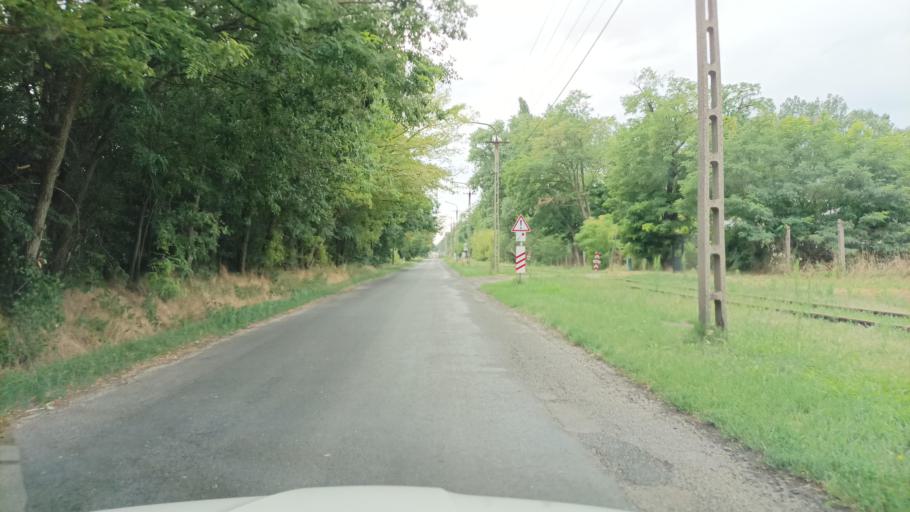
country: HU
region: Pest
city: Taborfalva
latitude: 47.0801
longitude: 19.4471
